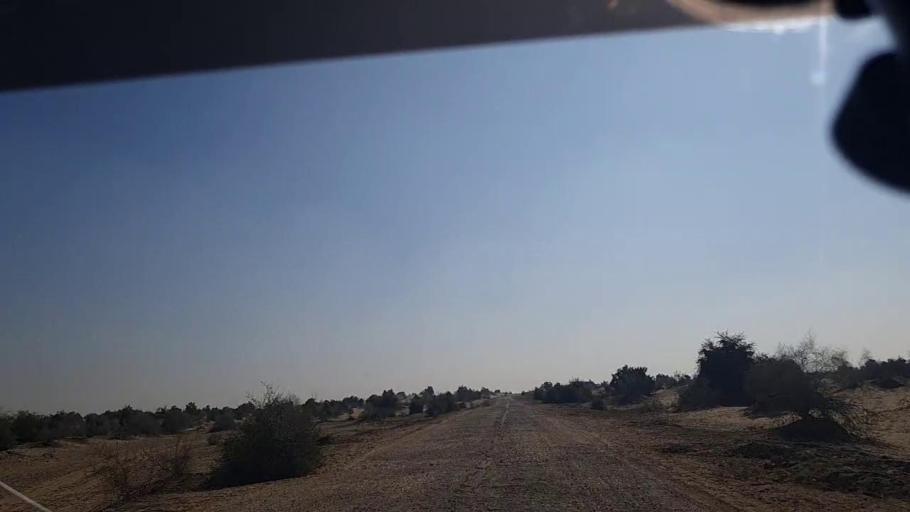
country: PK
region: Sindh
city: Khanpur
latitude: 27.5779
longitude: 69.3054
